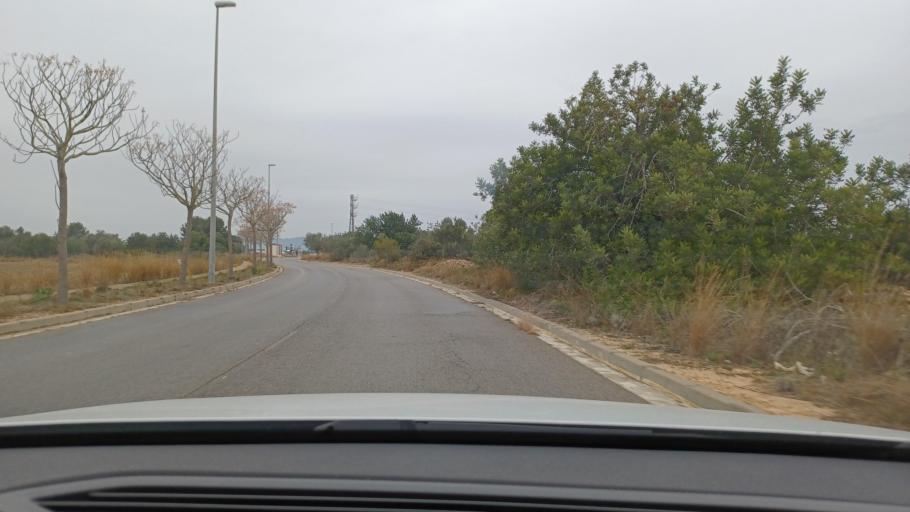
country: ES
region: Catalonia
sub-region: Provincia de Tarragona
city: Amposta
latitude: 40.7620
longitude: 0.5998
